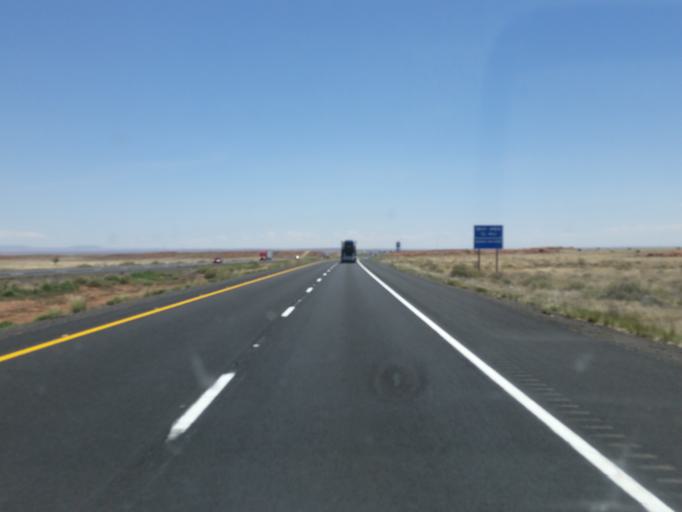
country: US
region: Arizona
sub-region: Coconino County
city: LeChee
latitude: 35.1089
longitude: -111.0219
